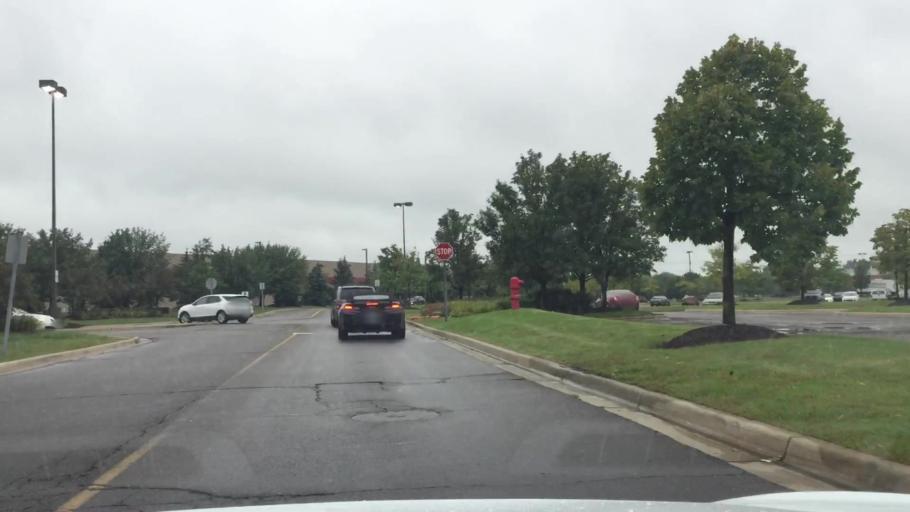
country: US
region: Michigan
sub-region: Wayne County
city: Livonia
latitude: 42.3803
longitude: -83.3297
